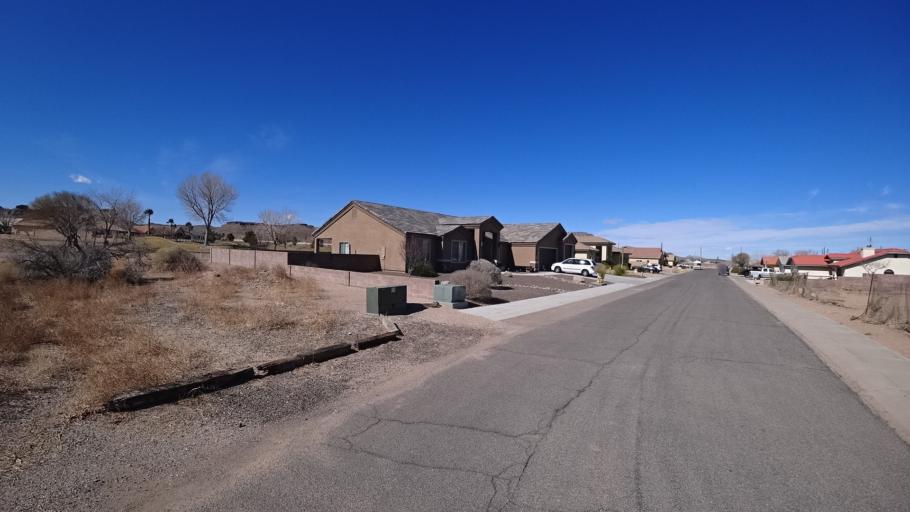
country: US
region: Arizona
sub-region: Mohave County
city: Kingman
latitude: 35.2131
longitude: -114.0435
